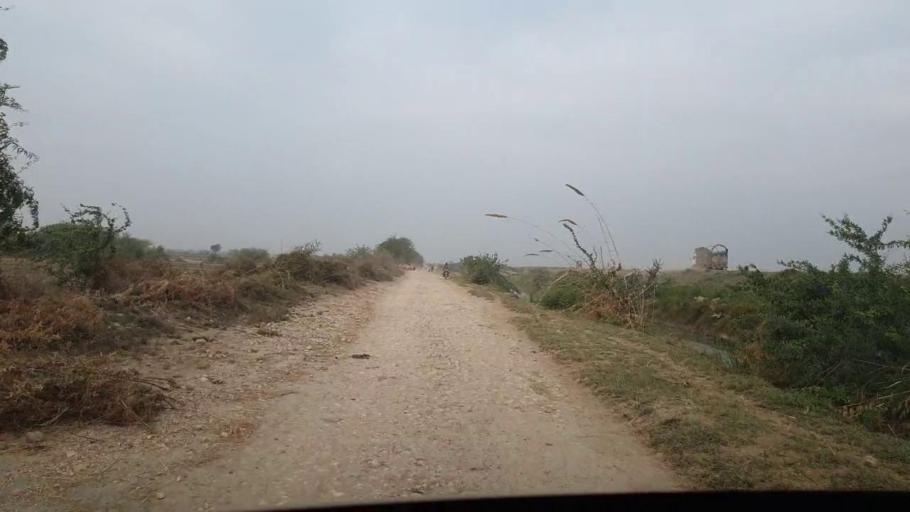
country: PK
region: Sindh
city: Chuhar Jamali
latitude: 24.4058
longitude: 67.9562
